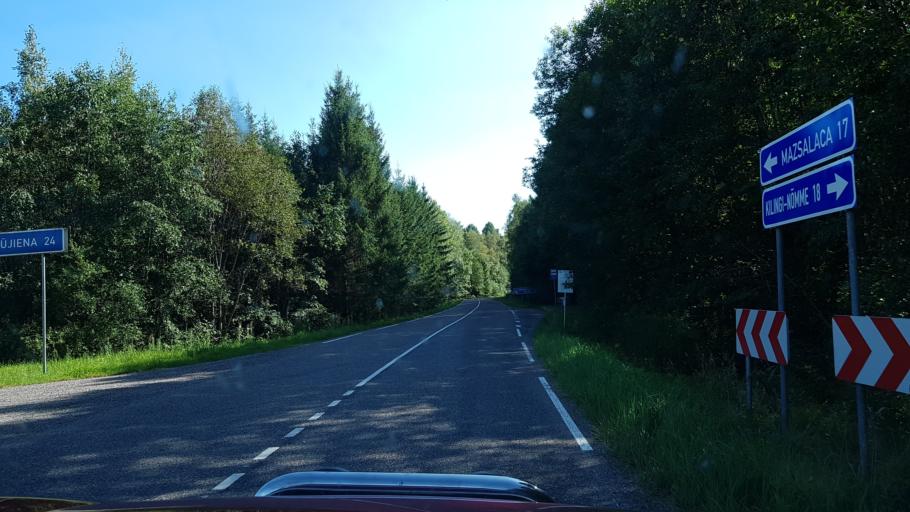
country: EE
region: Paernumaa
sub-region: Saarde vald
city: Kilingi-Nomme
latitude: 58.0144
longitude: 25.0094
